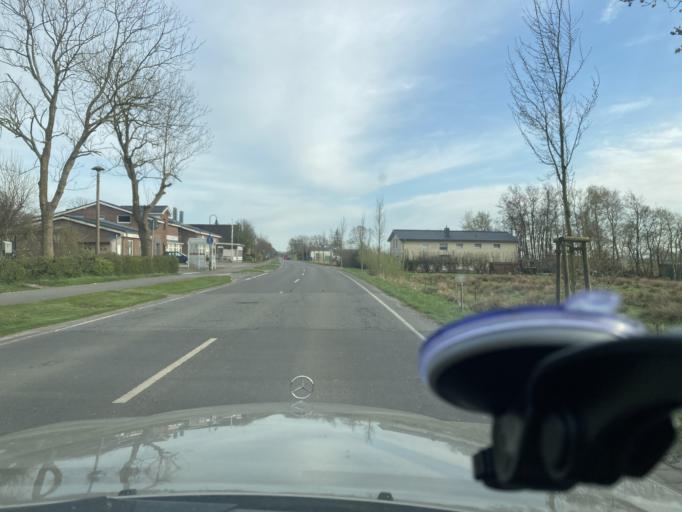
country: DE
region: Schleswig-Holstein
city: Krempel
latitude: 54.3193
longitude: 9.0280
